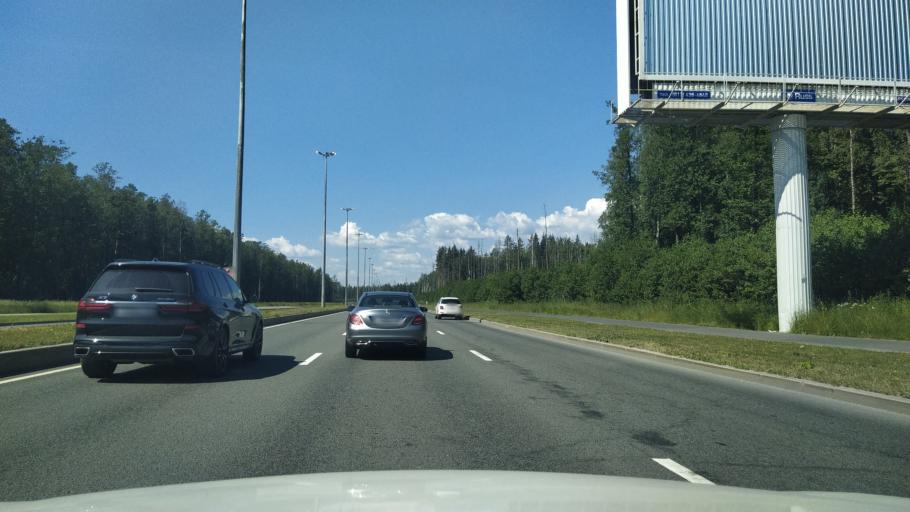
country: RU
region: Leningrad
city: Untolovo
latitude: 60.0571
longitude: 30.2222
